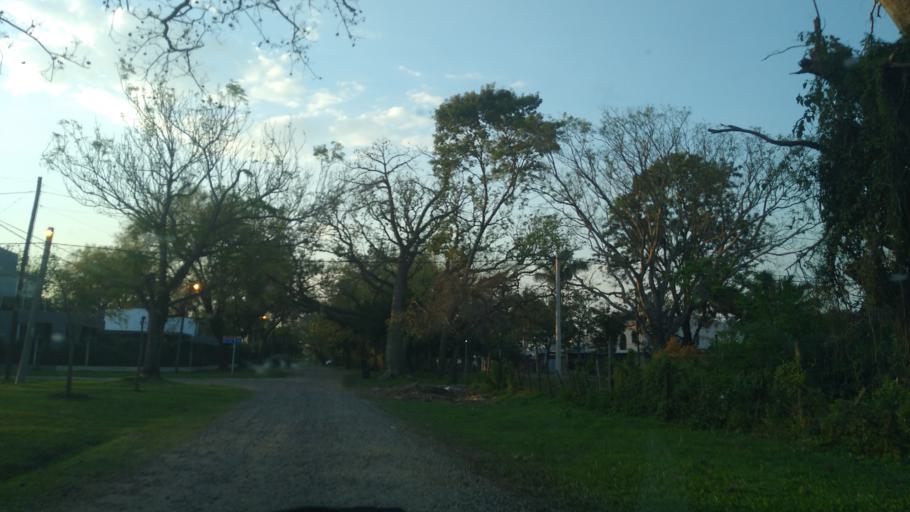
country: AR
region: Chaco
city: Barranqueras
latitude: -27.4683
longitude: -58.9563
